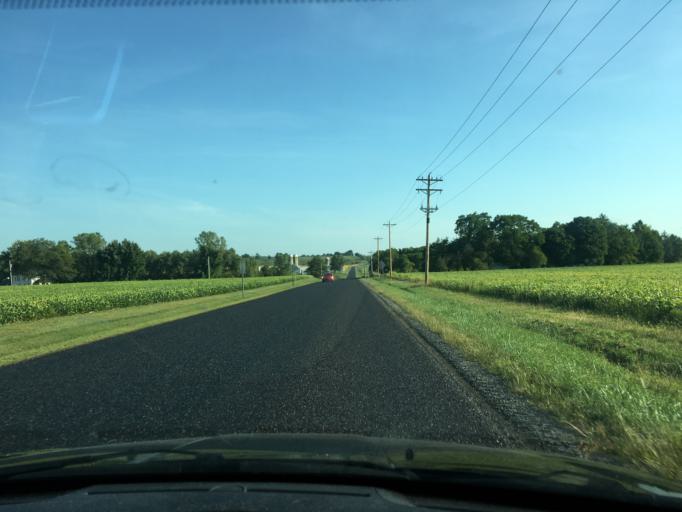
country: US
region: Ohio
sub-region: Logan County
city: West Liberty
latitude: 40.2844
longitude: -83.7270
